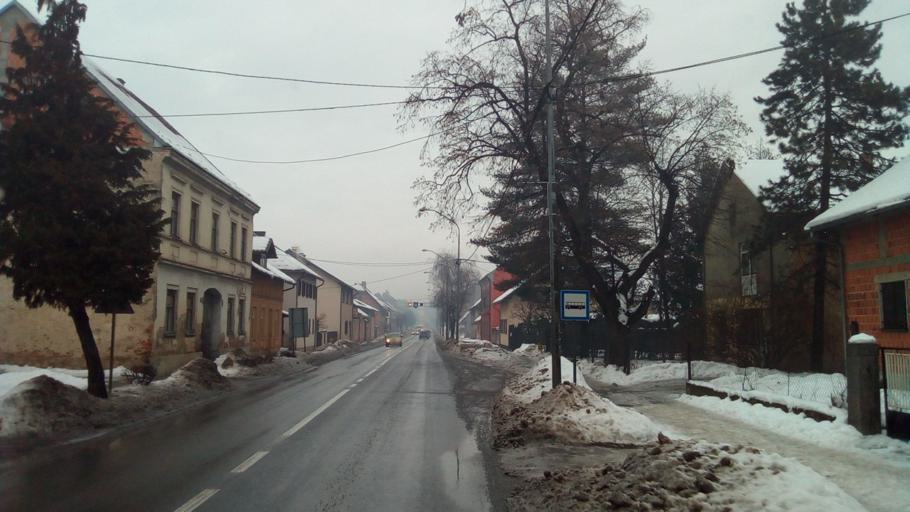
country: HR
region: Sisacko-Moslavacka
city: Petrinja
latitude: 45.4400
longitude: 16.2691
